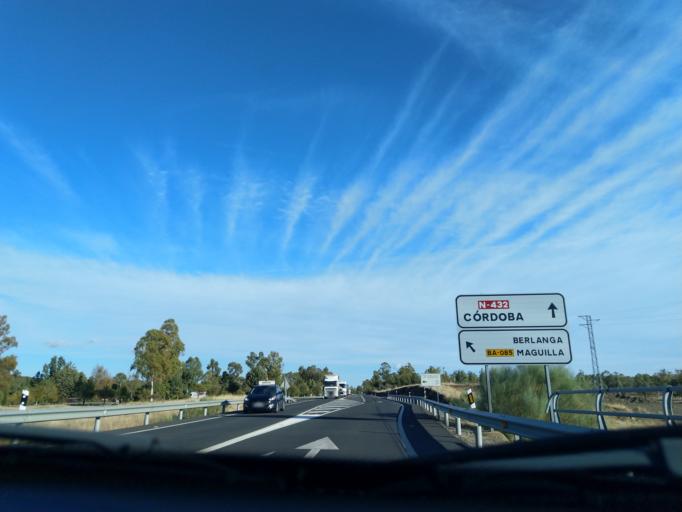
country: ES
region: Extremadura
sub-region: Provincia de Badajoz
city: Berlanga
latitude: 38.2754
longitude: -5.8221
